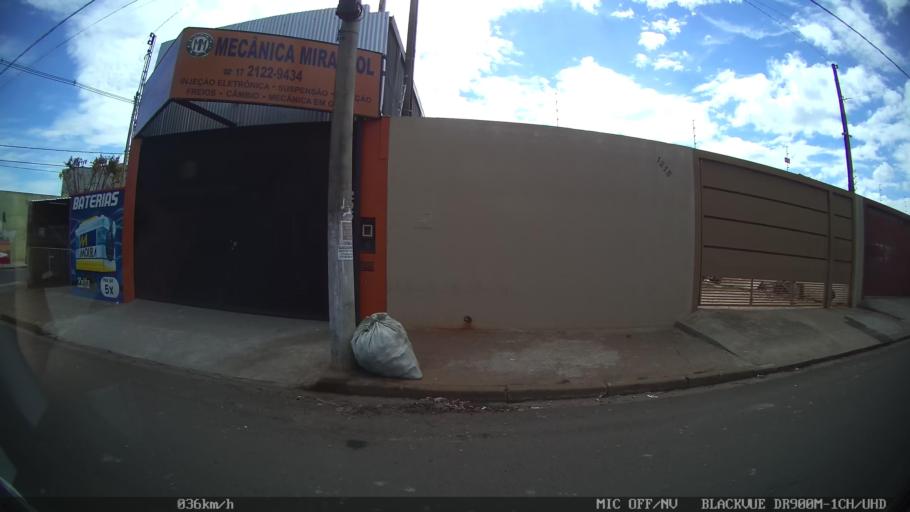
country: BR
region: Sao Paulo
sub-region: Bady Bassitt
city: Bady Bassitt
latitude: -20.8150
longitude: -49.5203
